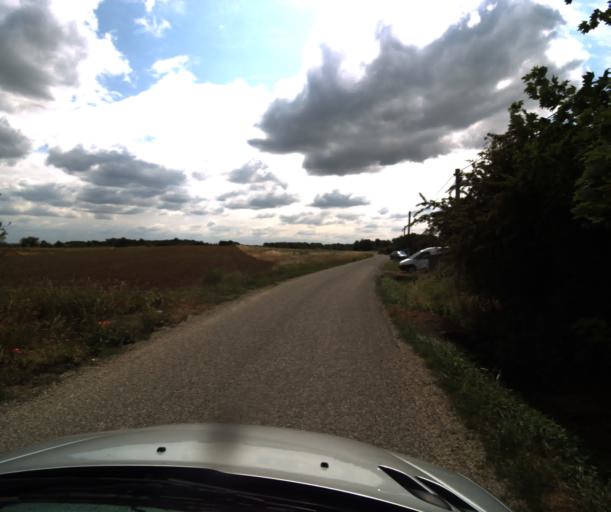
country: FR
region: Midi-Pyrenees
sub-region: Departement du Tarn-et-Garonne
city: Campsas
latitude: 43.9121
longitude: 1.2819
